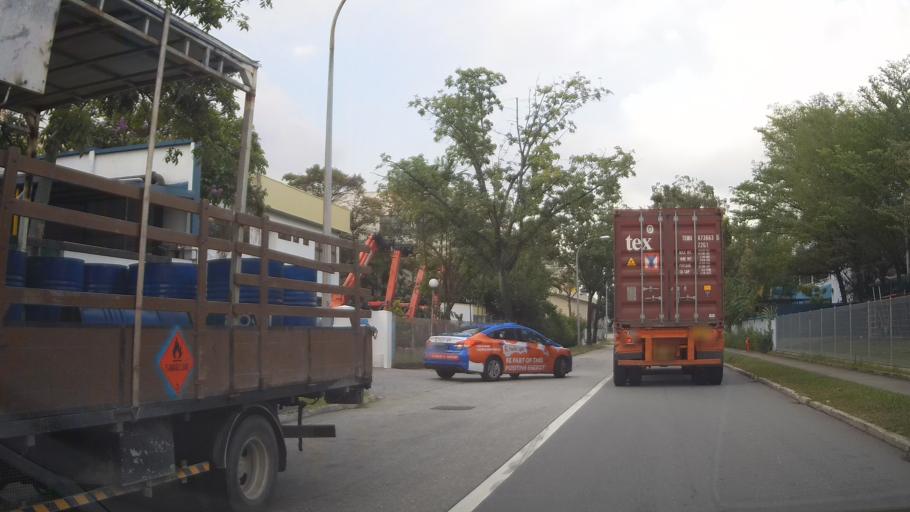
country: MY
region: Johor
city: Johor Bahru
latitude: 1.3231
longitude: 103.6419
